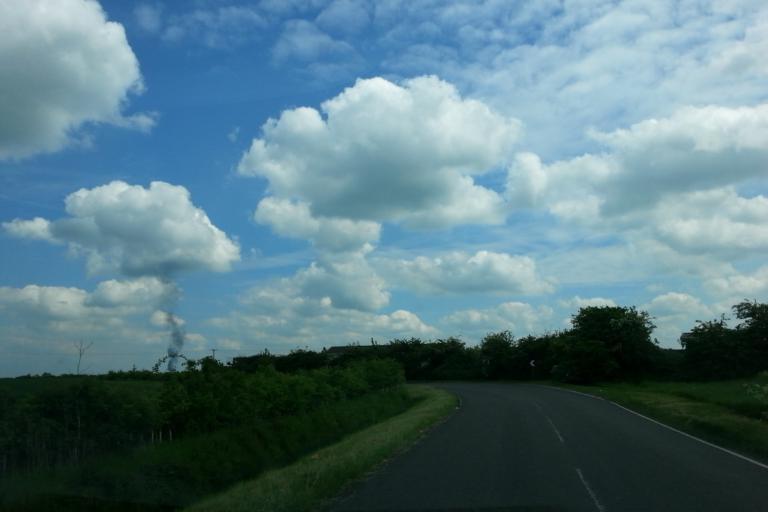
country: GB
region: England
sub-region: Cambridgeshire
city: Swavesey
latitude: 52.2889
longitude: -0.0178
